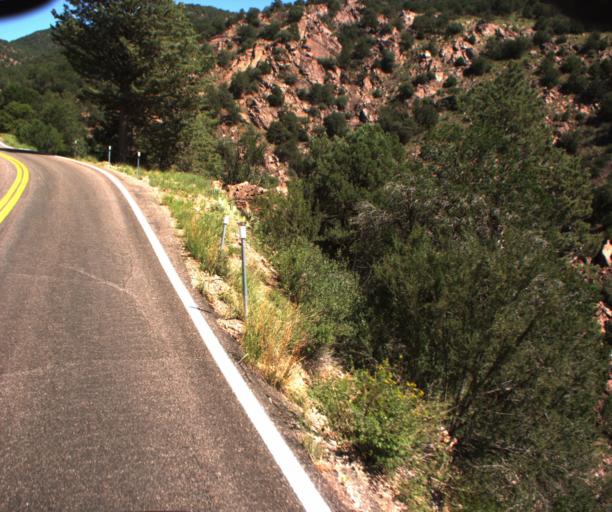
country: US
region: Arizona
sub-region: Greenlee County
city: Morenci
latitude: 33.1752
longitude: -109.3713
